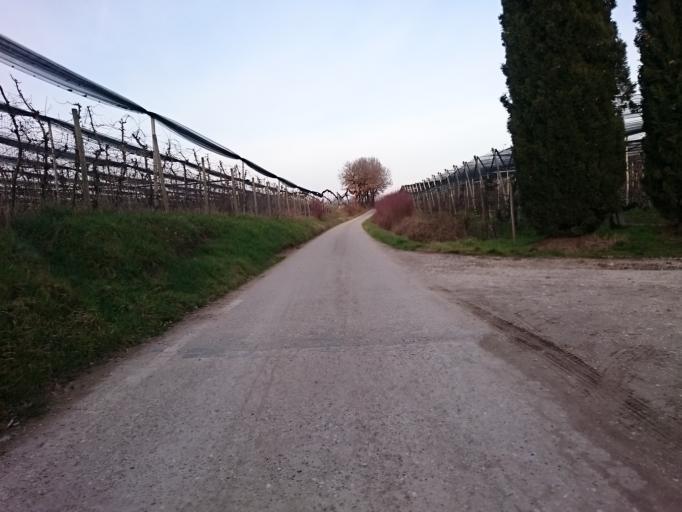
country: IT
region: Veneto
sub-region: Provincia di Verona
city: Cavalcaselle
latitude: 45.4502
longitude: 10.7308
